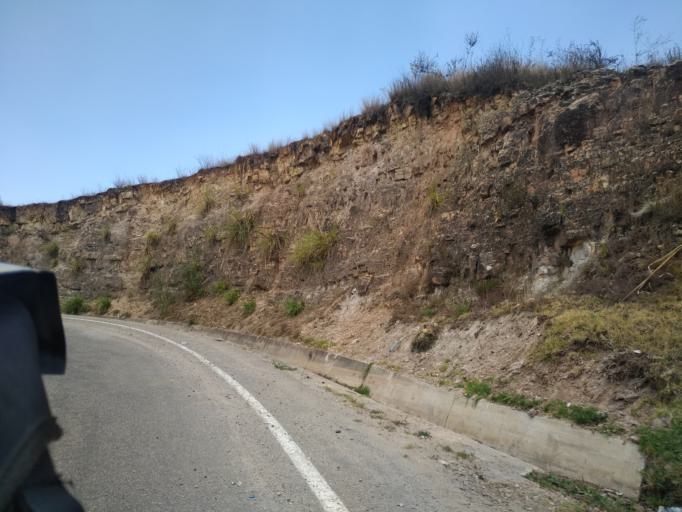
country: PE
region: Cajamarca
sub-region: San Marcos
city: San Marcos
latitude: -7.2836
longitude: -78.2229
